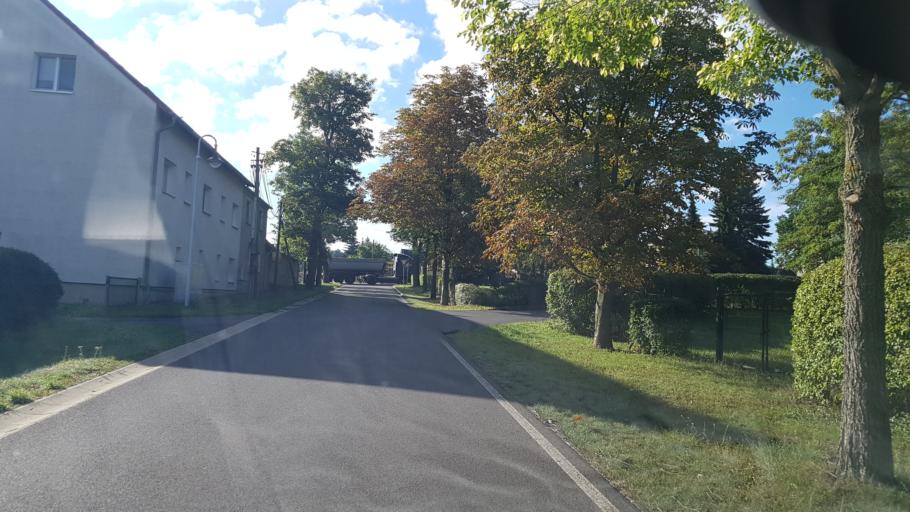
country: DE
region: Saxony
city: Gross Duben
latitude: 51.6233
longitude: 14.5355
